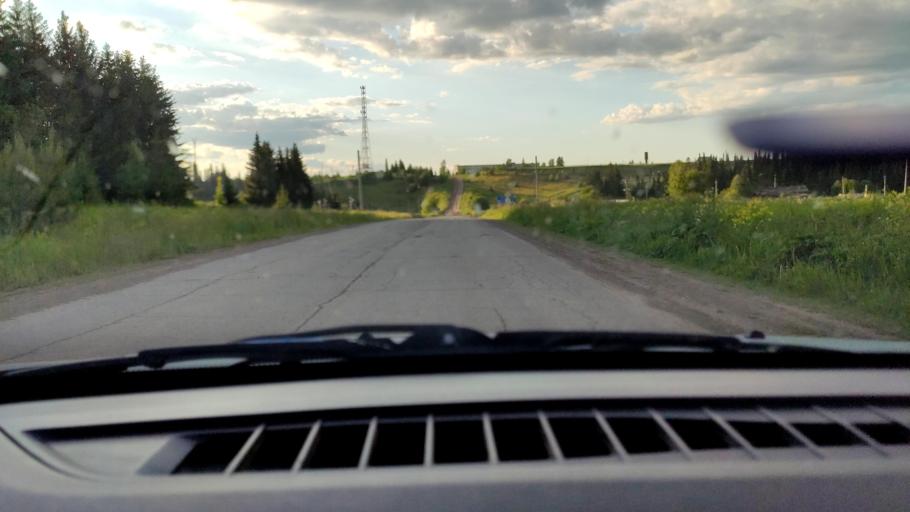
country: RU
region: Perm
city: Uinskoye
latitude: 57.1073
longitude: 56.5326
